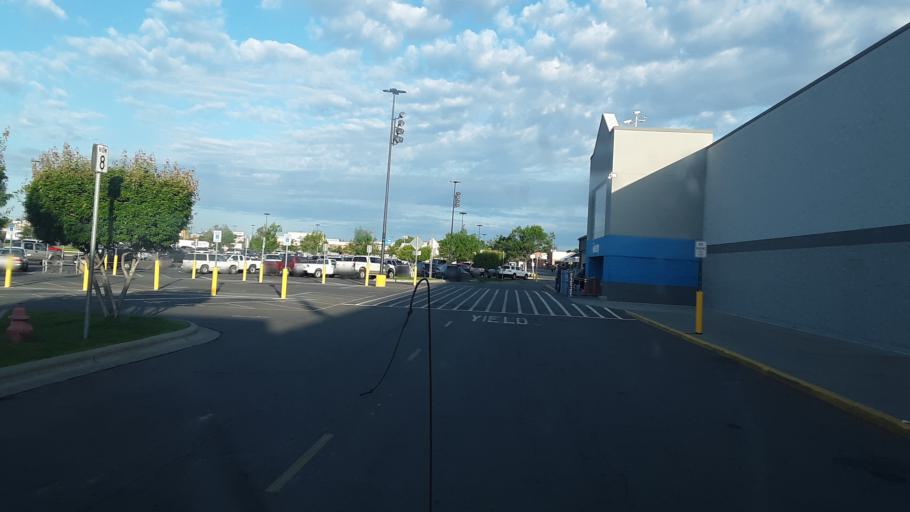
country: US
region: Montana
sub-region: Yellowstone County
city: Billings
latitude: 45.7575
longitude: -108.5795
